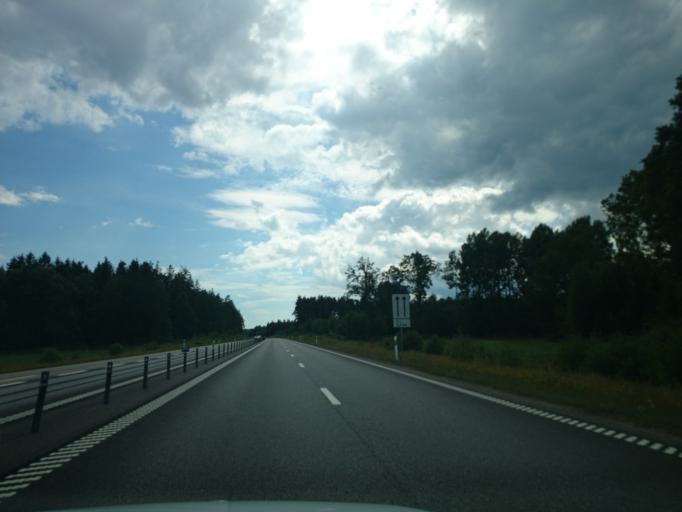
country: SE
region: Kalmar
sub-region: Kalmar Kommun
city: Ljungbyholm
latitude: 56.5499
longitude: 16.0851
